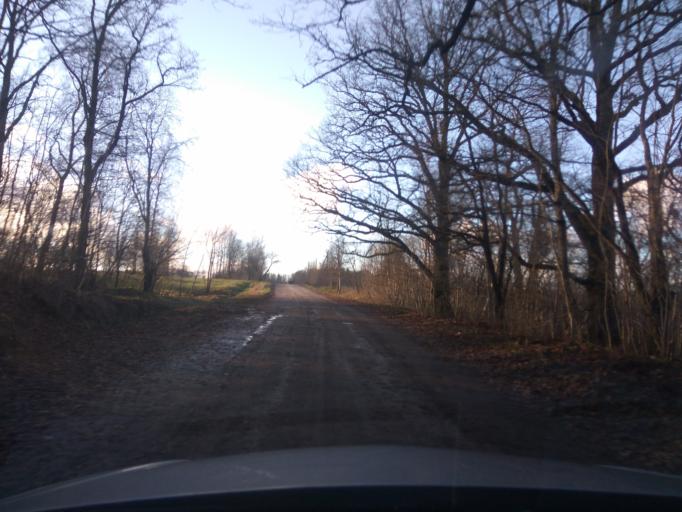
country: LV
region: Aizpute
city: Aizpute
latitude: 56.7480
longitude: 21.5994
